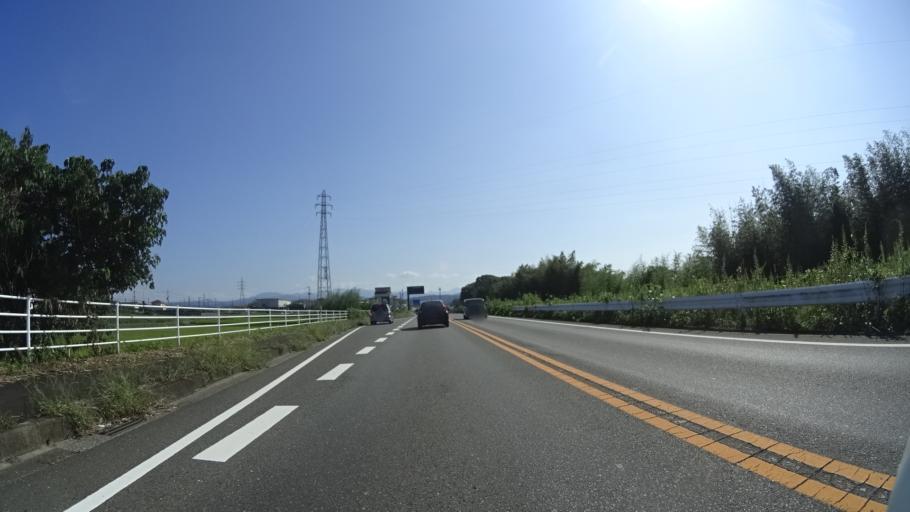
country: JP
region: Fukuoka
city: Yukuhashi
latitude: 33.6880
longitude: 130.9971
